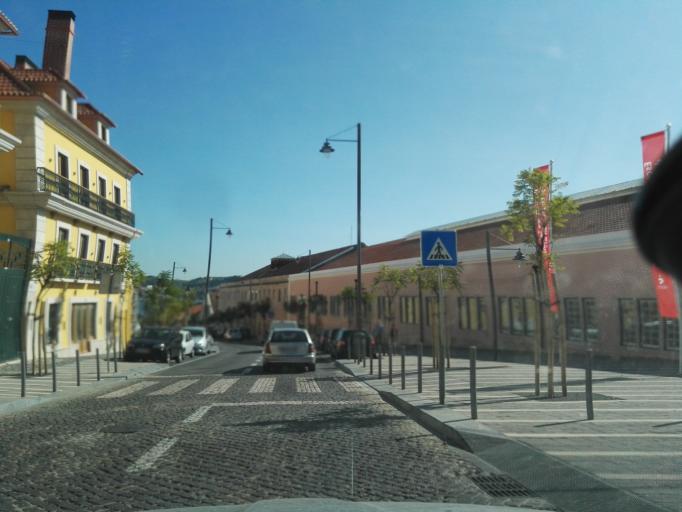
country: PT
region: Lisbon
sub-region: Oeiras
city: Alges
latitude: 38.7006
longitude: -9.1999
